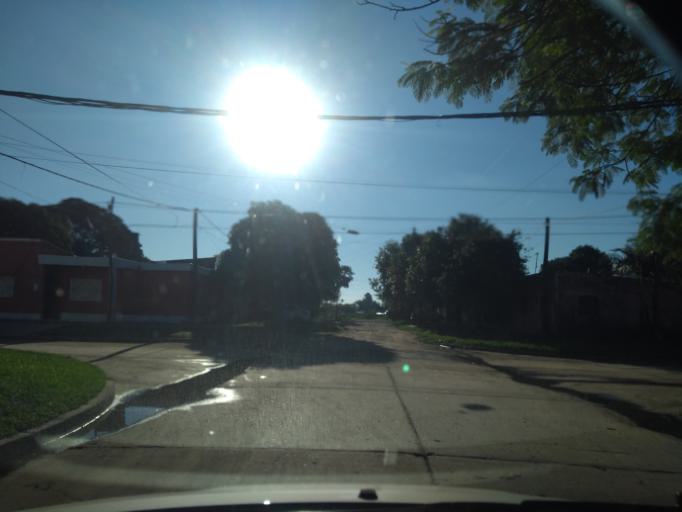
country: AR
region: Chaco
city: Barranqueras
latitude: -27.4805
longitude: -58.9368
